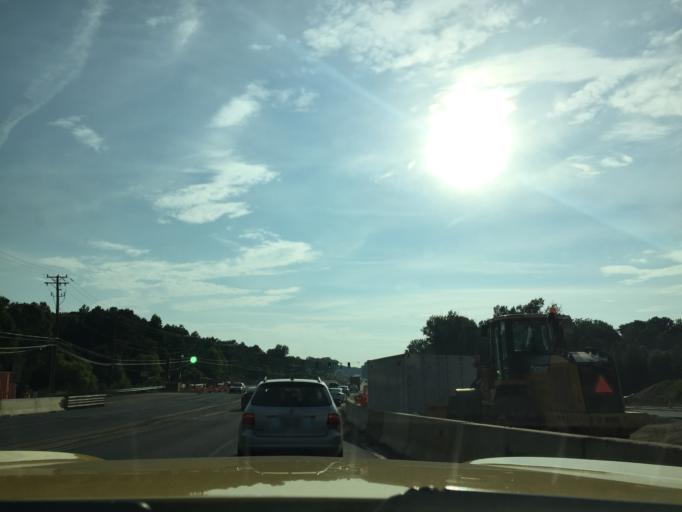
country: US
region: Virginia
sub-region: Fairfax County
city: Fort Belvoir
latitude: 38.7082
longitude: -77.1625
